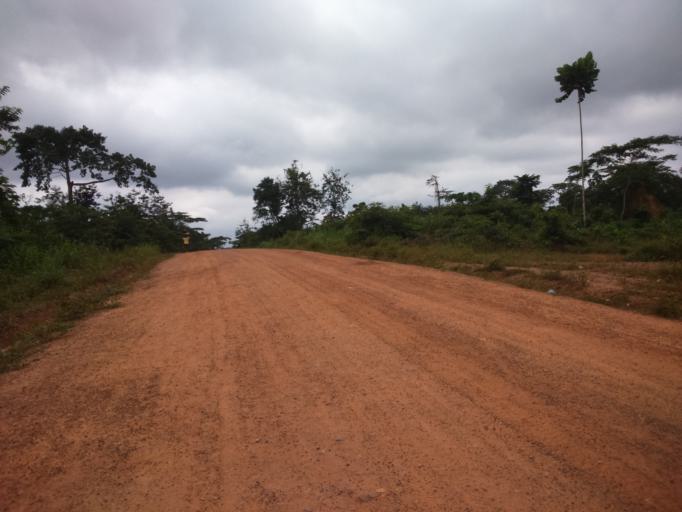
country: CI
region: Lagunes
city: Agou
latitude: 6.0794
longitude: -4.0670
